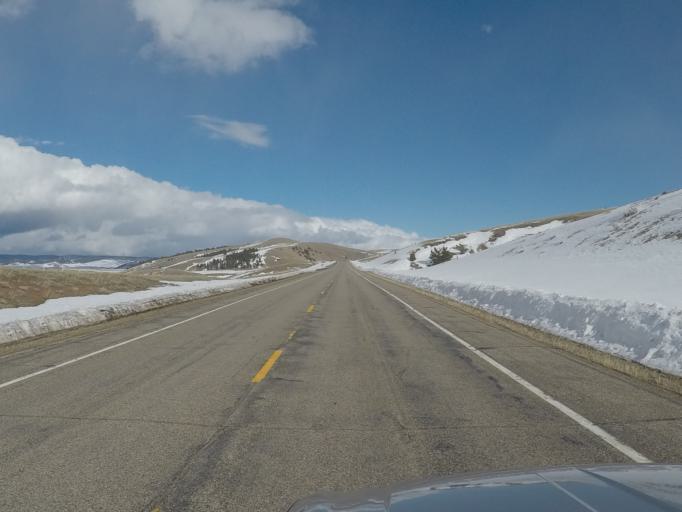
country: US
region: Montana
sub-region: Meagher County
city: White Sulphur Springs
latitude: 46.6217
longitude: -110.7158
